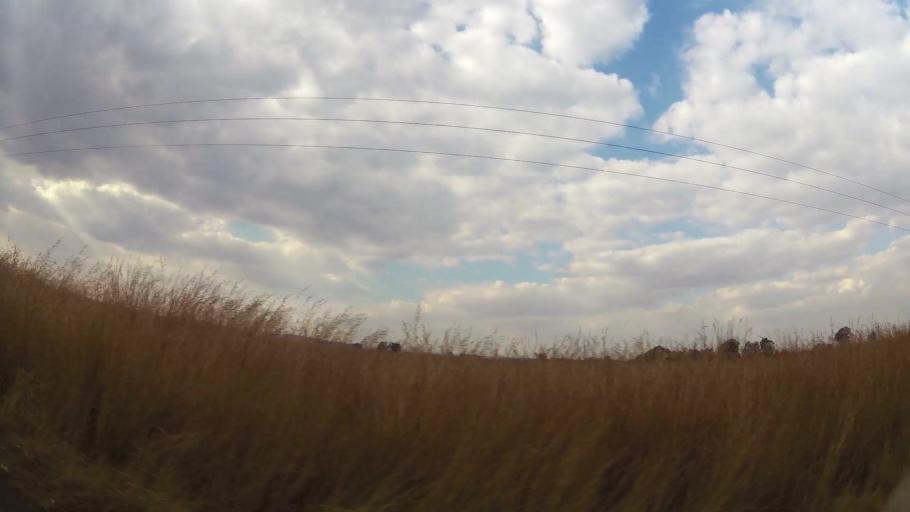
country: ZA
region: Mpumalanga
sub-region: Nkangala District Municipality
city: Delmas
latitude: -26.2386
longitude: 28.6311
